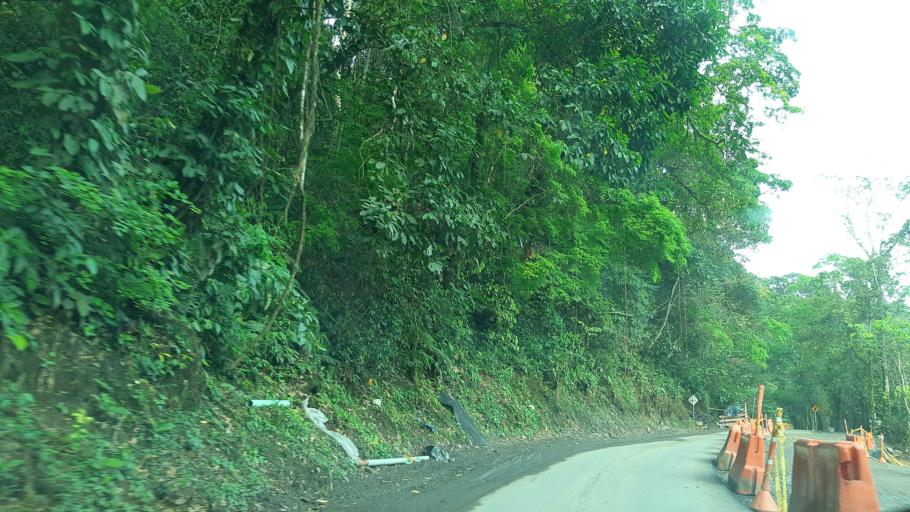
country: CO
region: Boyaca
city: Santa Maria
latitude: 4.8438
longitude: -73.2176
